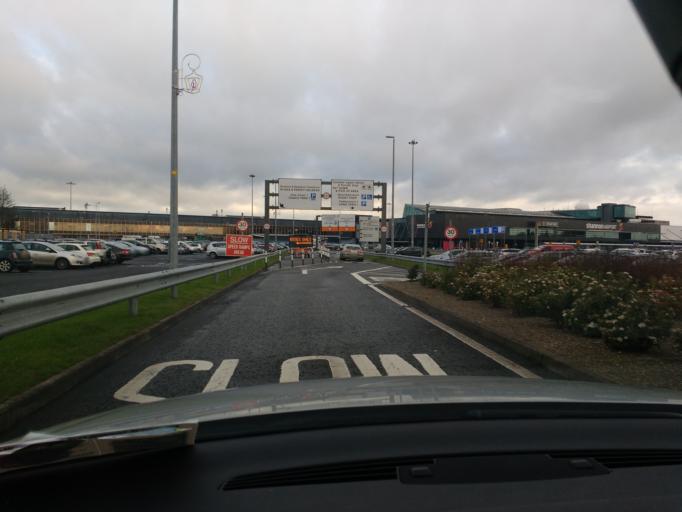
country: IE
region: Munster
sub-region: An Clar
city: Shannon
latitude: 52.6914
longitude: -8.9239
